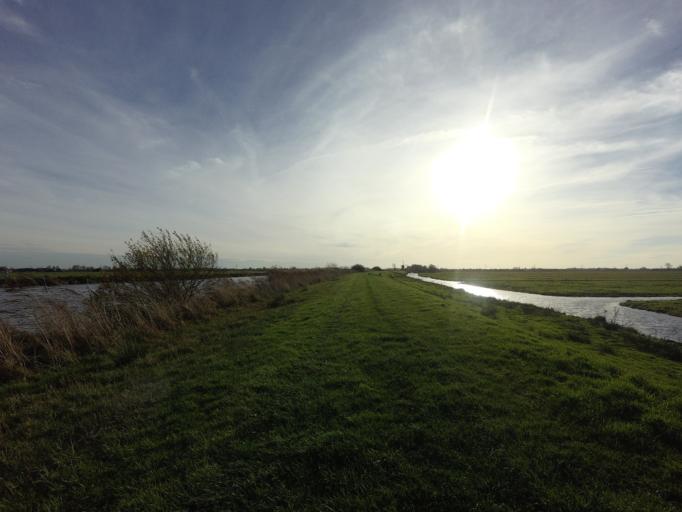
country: NL
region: South Holland
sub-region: Gemeente Vlist
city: Haastrecht
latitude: 52.0384
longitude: 4.7849
